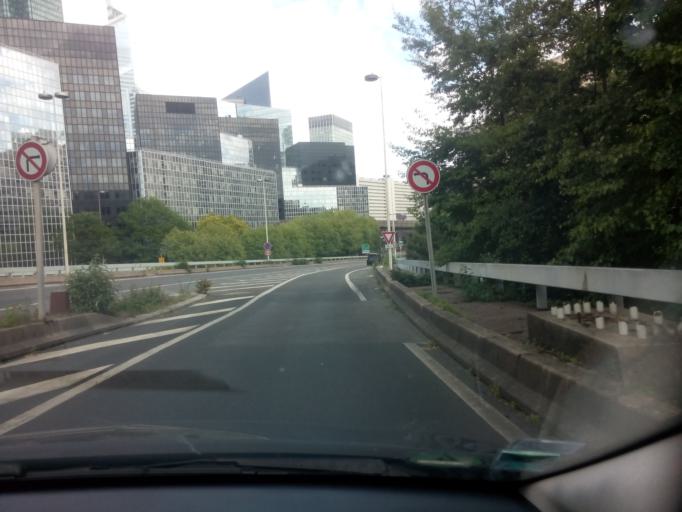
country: FR
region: Ile-de-France
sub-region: Departement des Hauts-de-Seine
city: Puteaux
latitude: 48.8870
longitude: 2.2433
